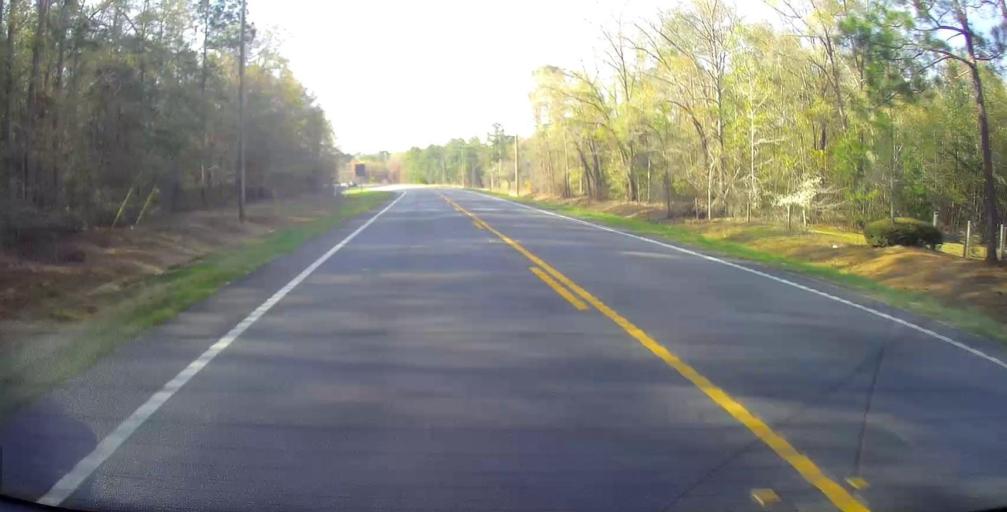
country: US
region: Georgia
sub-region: Montgomery County
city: Mount Vernon
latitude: 32.1896
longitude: -82.6131
